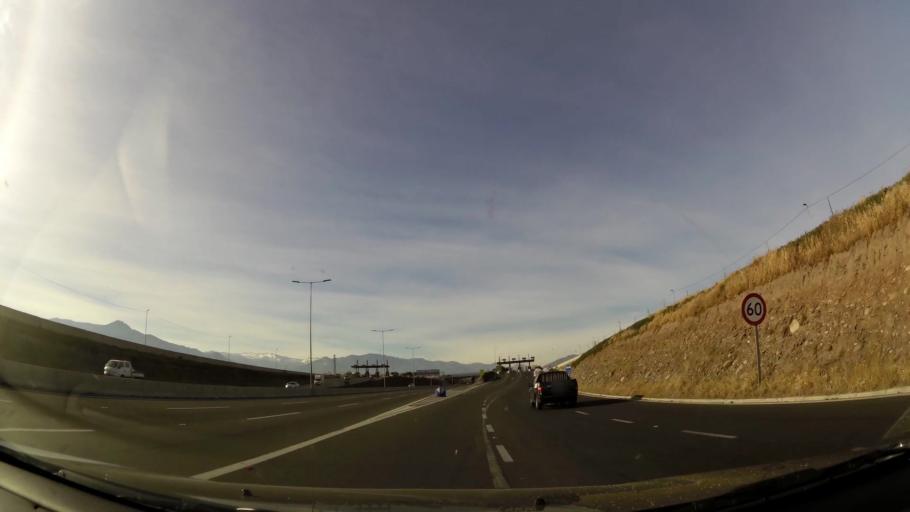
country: CL
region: Santiago Metropolitan
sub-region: Provincia de Cordillera
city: Puente Alto
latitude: -33.6033
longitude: -70.6049
